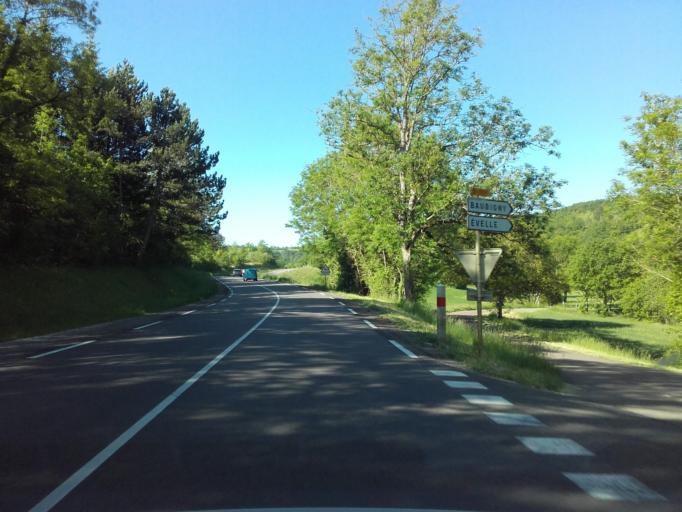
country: FR
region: Bourgogne
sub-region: Departement de la Cote-d'Or
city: Nolay
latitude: 46.9712
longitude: 4.6984
